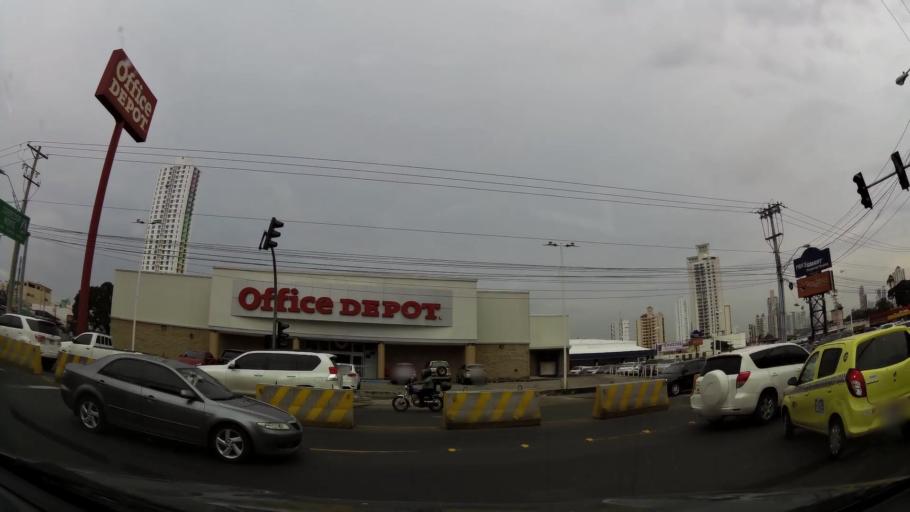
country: PA
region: Panama
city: Panama
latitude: 8.9911
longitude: -79.5203
